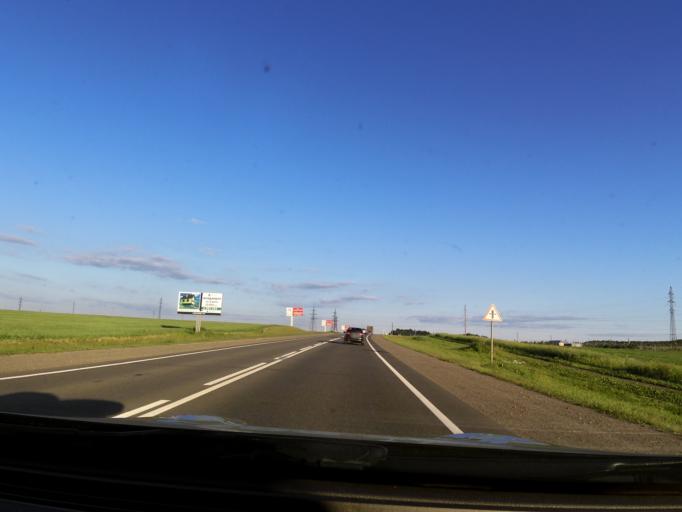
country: RU
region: Vologda
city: Vologda
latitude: 59.1622
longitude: 39.9241
